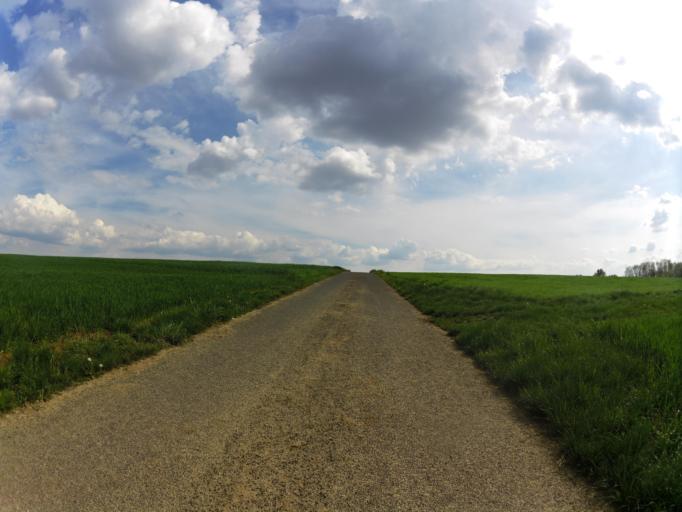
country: DE
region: Bavaria
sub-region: Regierungsbezirk Unterfranken
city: Giebelstadt
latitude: 49.6225
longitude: 9.9407
